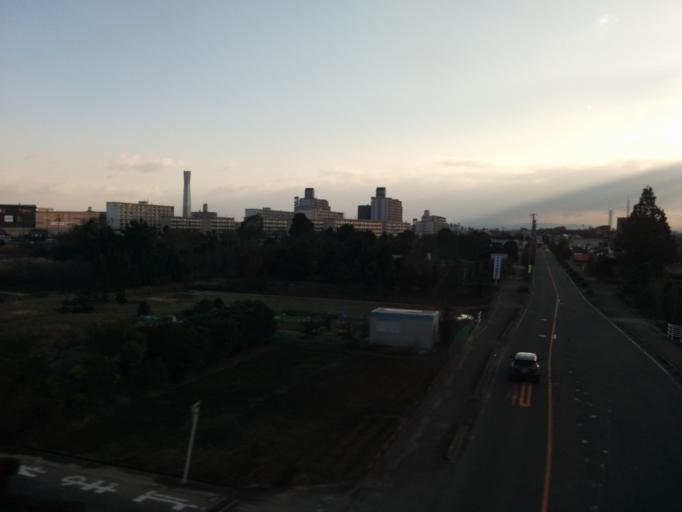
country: JP
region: Aichi
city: Inazawa
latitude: 35.2487
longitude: 136.7697
